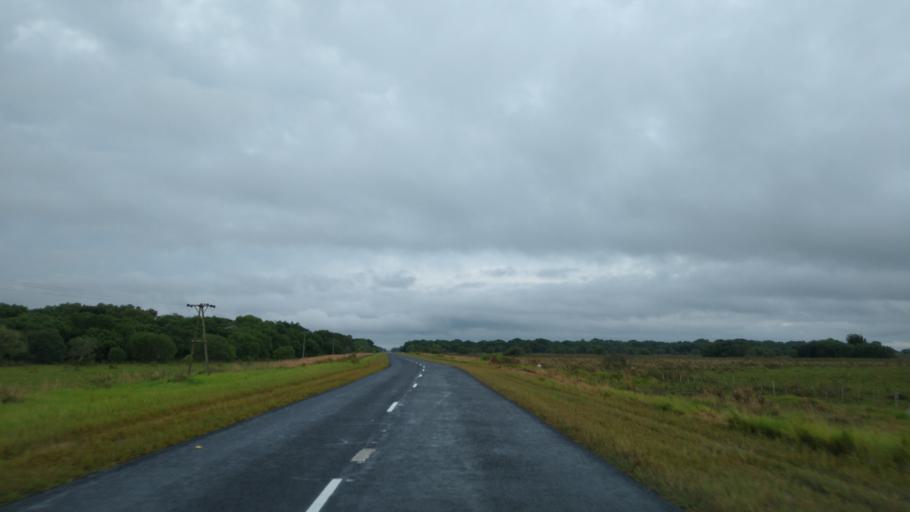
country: AR
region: Corrientes
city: Loreto
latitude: -27.7534
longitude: -57.2576
